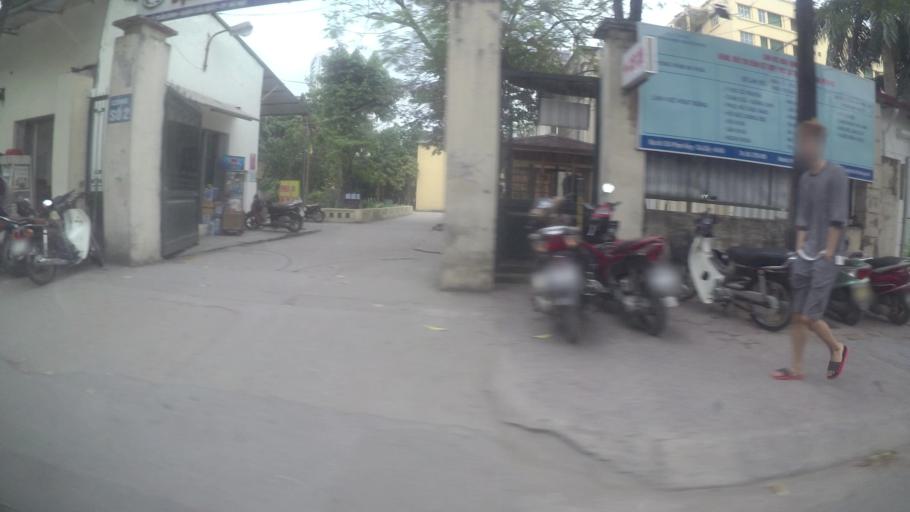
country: VN
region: Ha Noi
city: Cau Dien
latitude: 21.0347
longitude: 105.7789
